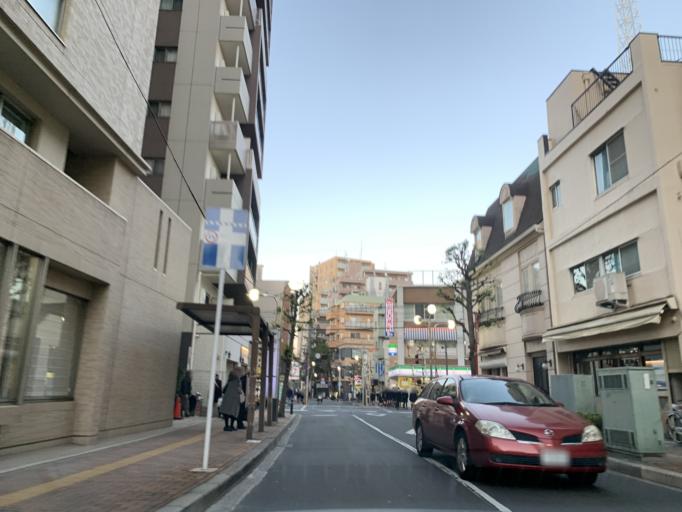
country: JP
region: Chiba
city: Matsudo
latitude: 35.7319
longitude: 139.9103
